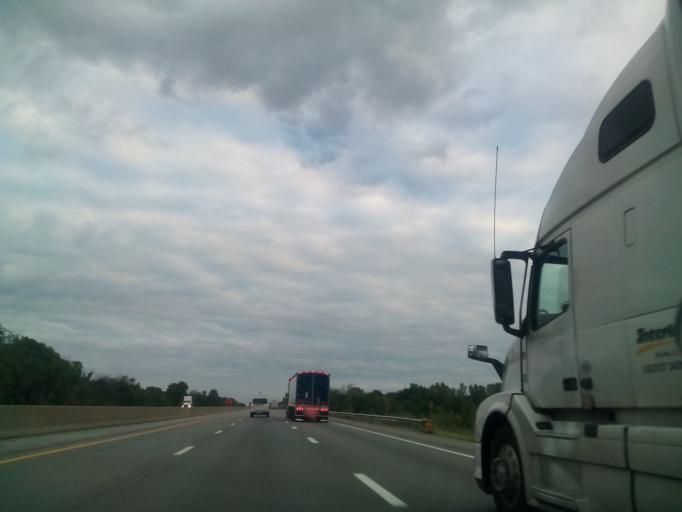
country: US
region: Ohio
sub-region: Trumbull County
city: Lordstown
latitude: 41.1701
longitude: -80.9137
